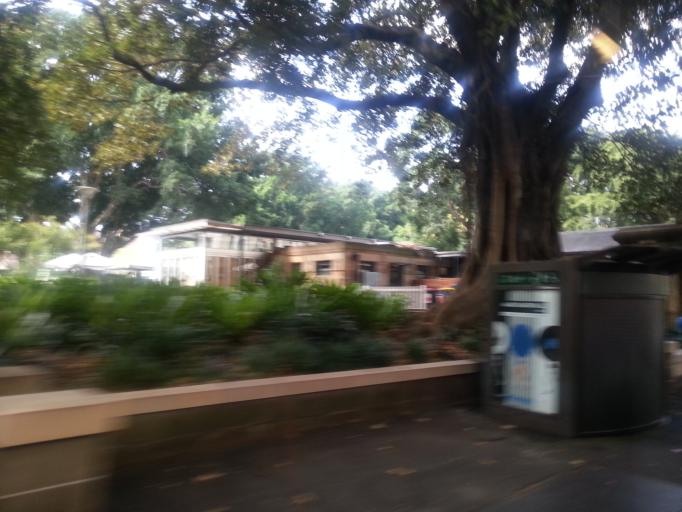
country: AU
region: New South Wales
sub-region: City of Sydney
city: Sydney
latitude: -33.8703
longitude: 151.2106
